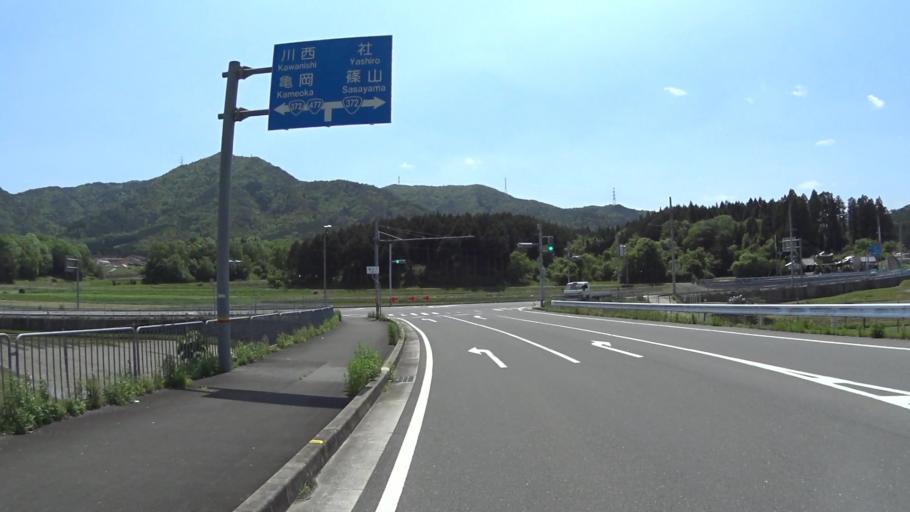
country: JP
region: Kyoto
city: Kameoka
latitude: 35.0626
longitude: 135.4551
